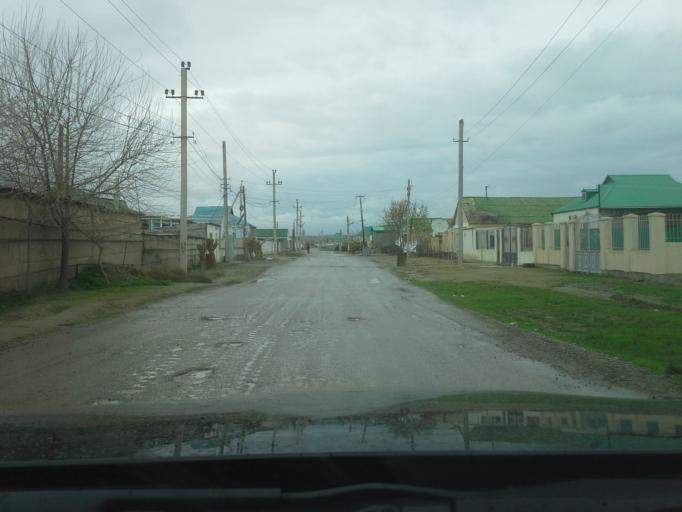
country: TM
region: Ahal
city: Abadan
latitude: 37.9702
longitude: 58.2118
